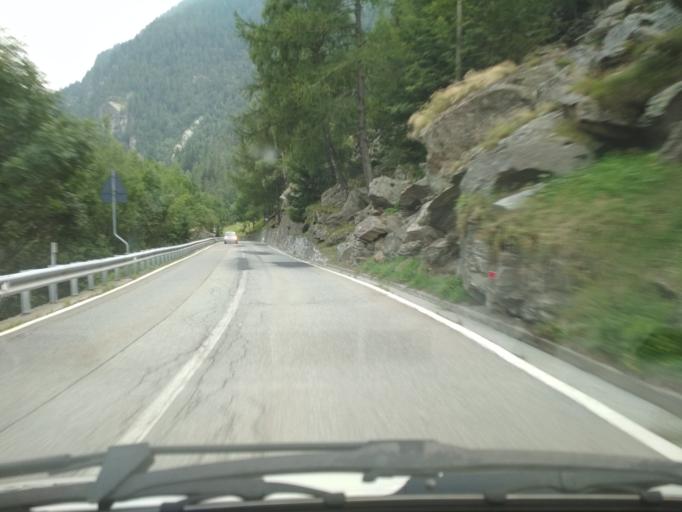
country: IT
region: Aosta Valley
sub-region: Valle d'Aosta
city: Gaby
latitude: 45.7311
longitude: 7.8562
